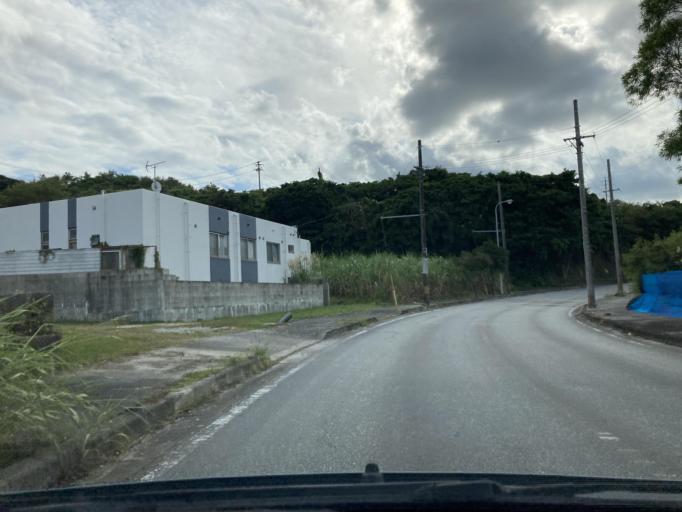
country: JP
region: Okinawa
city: Itoman
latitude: 26.1340
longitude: 127.7096
